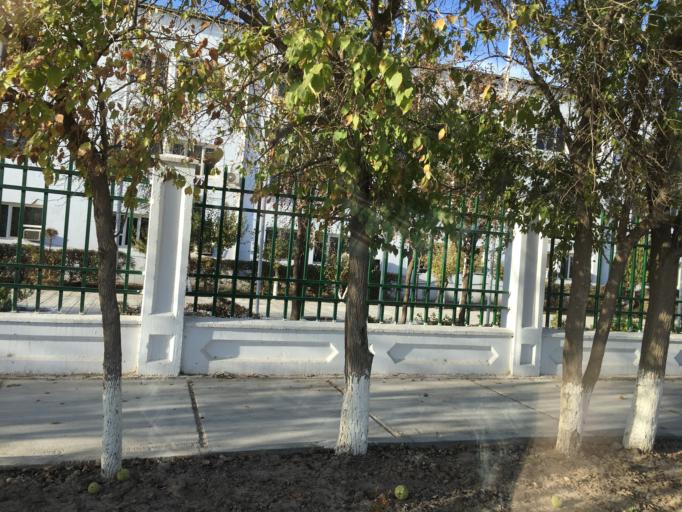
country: TM
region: Ahal
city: Tejen
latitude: 37.6917
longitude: 60.3935
